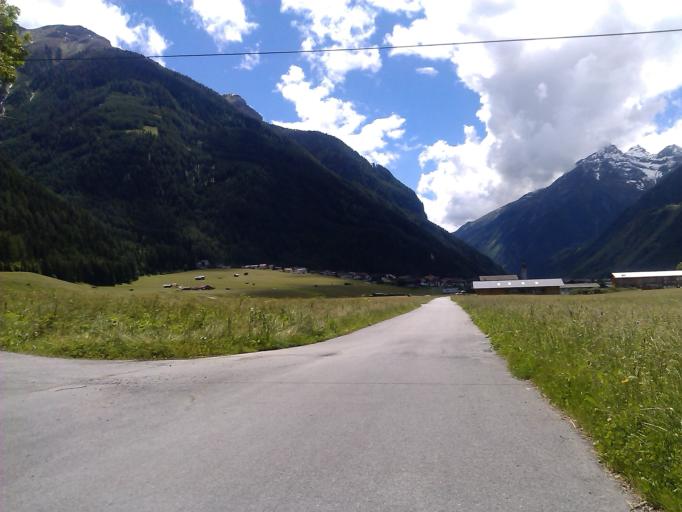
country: AT
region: Tyrol
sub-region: Politischer Bezirk Landeck
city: Pfunds
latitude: 46.9753
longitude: 10.5545
